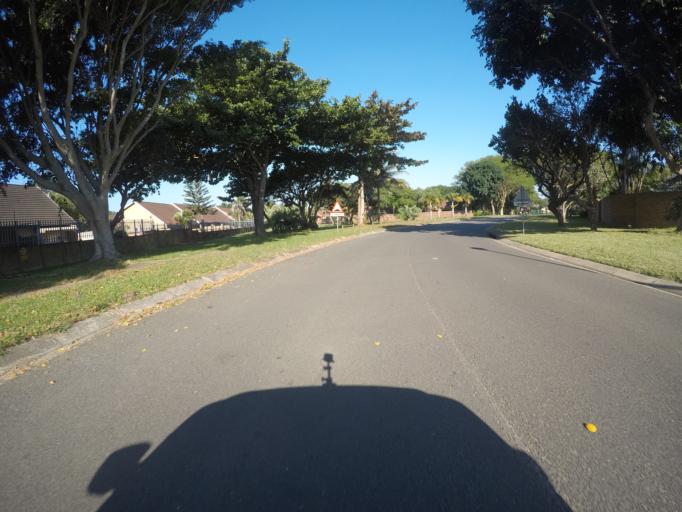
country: ZA
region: KwaZulu-Natal
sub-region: uThungulu District Municipality
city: Richards Bay
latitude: -28.7873
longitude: 32.1003
